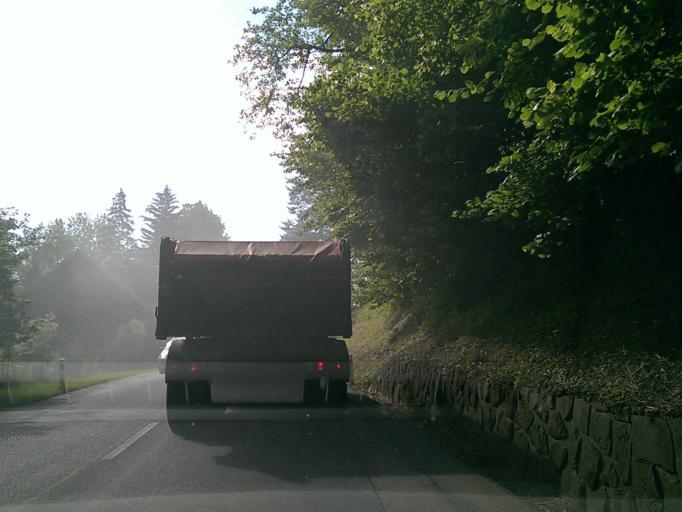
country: CZ
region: Liberecky
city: Rovensko pod Troskami
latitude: 50.5851
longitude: 15.2380
